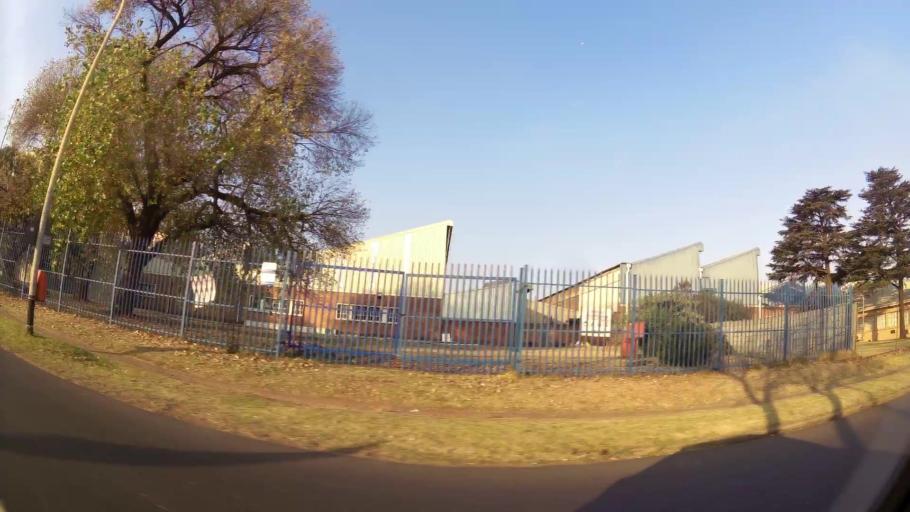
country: ZA
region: Gauteng
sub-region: Ekurhuleni Metropolitan Municipality
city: Springs
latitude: -26.2599
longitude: 28.4187
